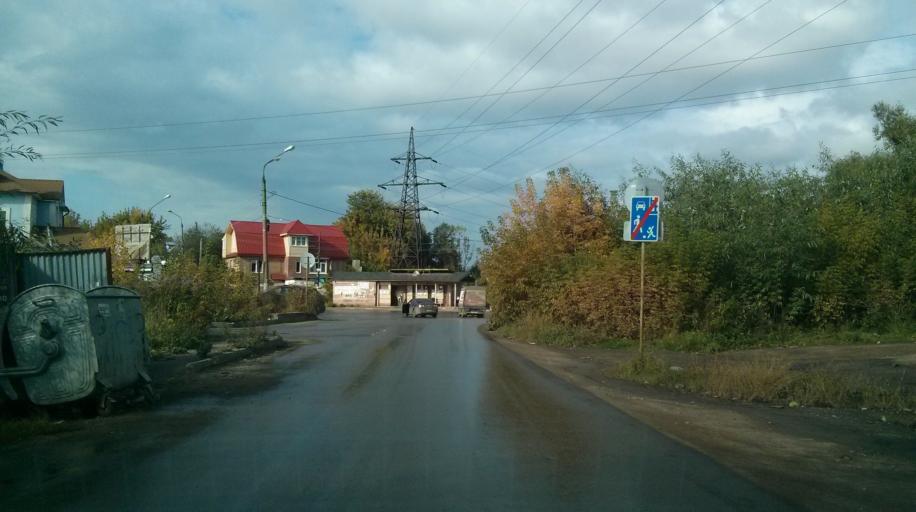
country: RU
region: Nizjnij Novgorod
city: Nizhniy Novgorod
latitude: 56.3078
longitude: 44.0445
